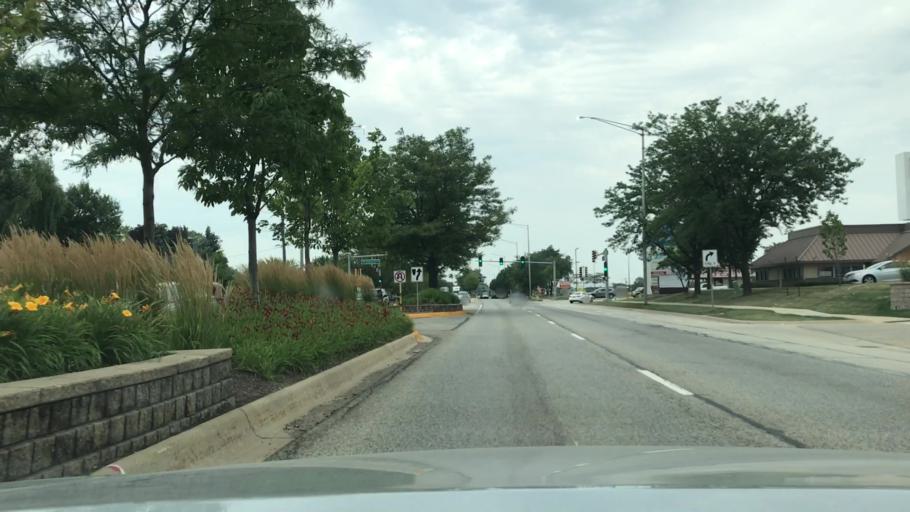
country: US
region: Illinois
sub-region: Will County
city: Bolingbrook
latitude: 41.6950
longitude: -88.0681
